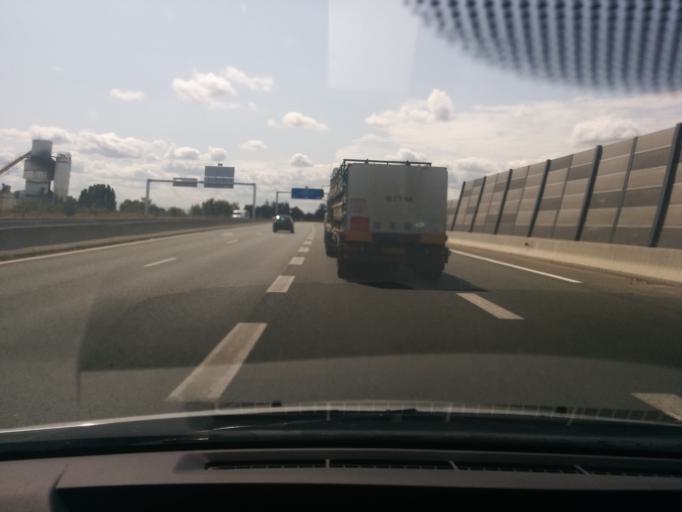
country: FR
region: Pays de la Loire
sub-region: Departement de Maine-et-Loire
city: Angers
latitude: 47.4645
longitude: -0.5169
